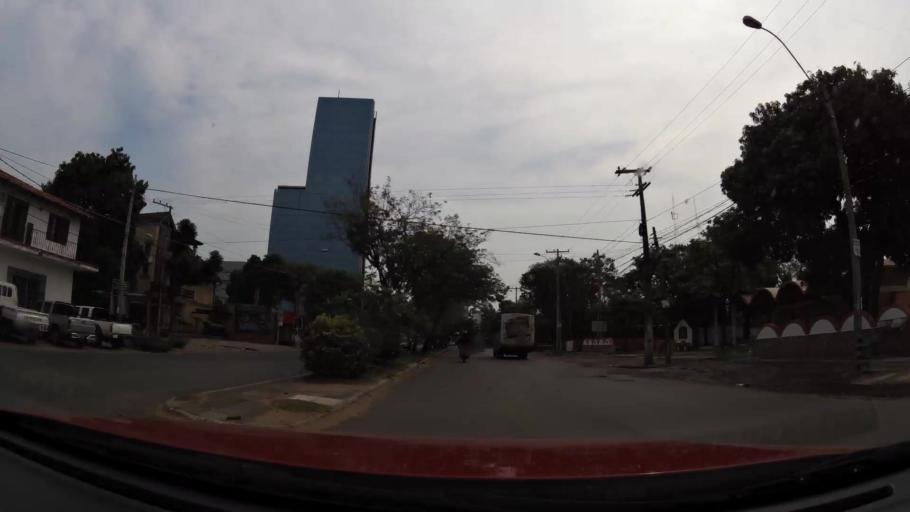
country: PY
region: Central
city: Fernando de la Mora
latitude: -25.2781
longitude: -57.5547
